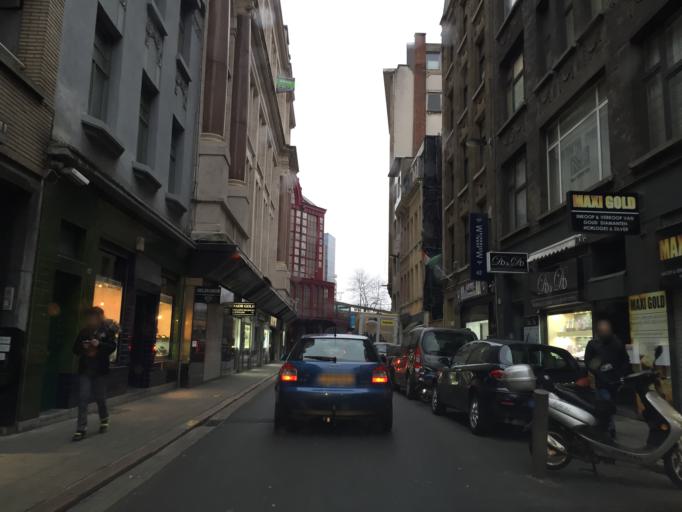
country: BE
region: Flanders
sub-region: Provincie Antwerpen
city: Antwerpen
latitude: 51.2160
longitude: 4.4197
